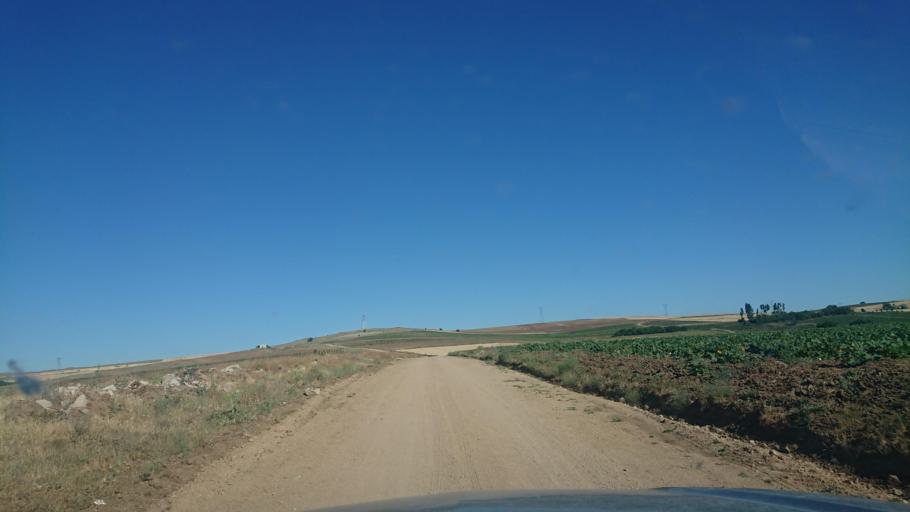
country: TR
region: Aksaray
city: Agacoren
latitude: 38.8274
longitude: 33.9548
